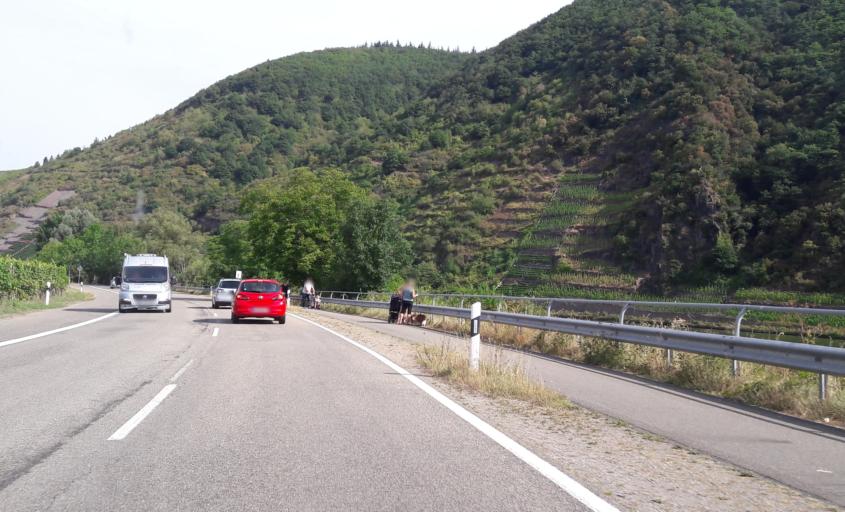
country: DE
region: Rheinland-Pfalz
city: Ellenz-Poltersdorf
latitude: 50.1110
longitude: 7.2366
